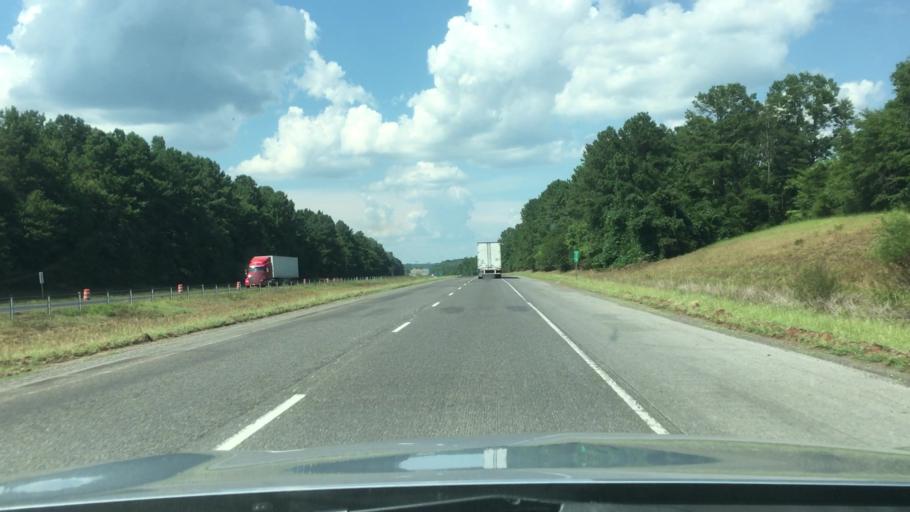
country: US
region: Alabama
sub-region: Sumter County
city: Livingston
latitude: 32.5980
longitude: -88.2225
